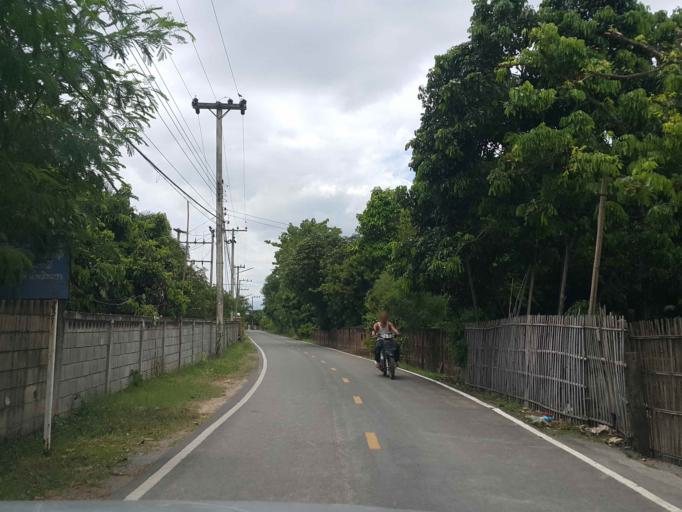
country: TH
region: Lamphun
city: Pa Sang
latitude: 18.4653
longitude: 98.9159
